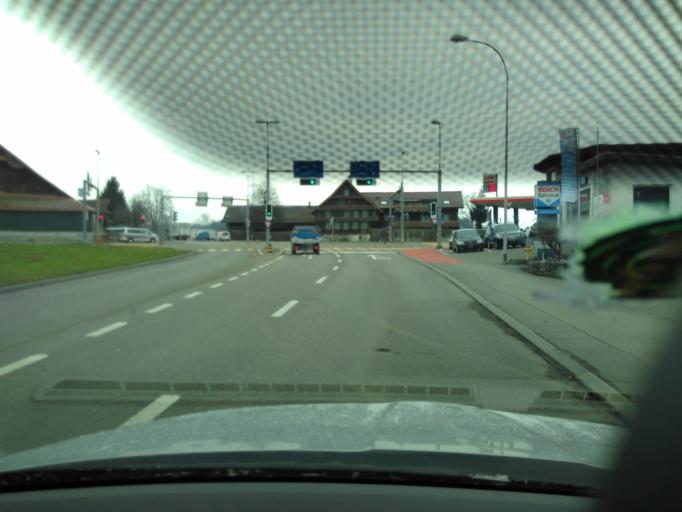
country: CH
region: Lucerne
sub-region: Hochdorf District
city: Inwil
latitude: 47.1212
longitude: 8.3415
